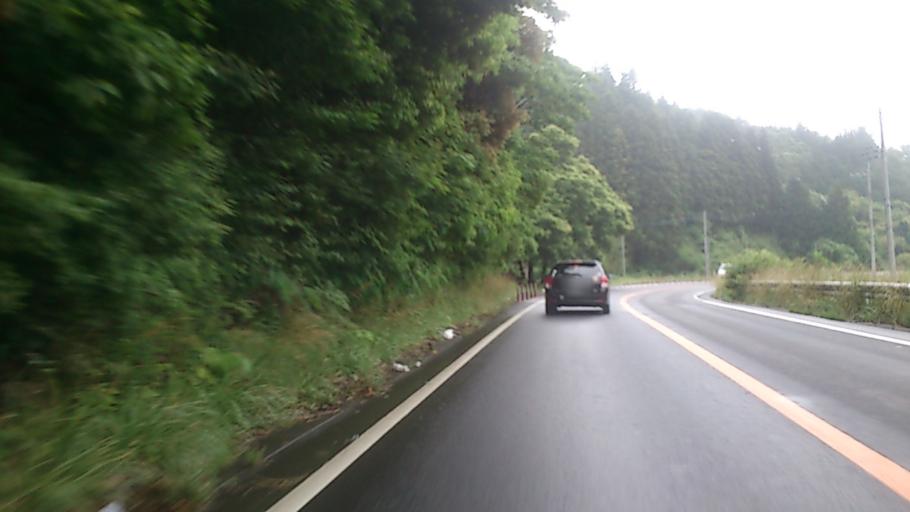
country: JP
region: Tochigi
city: Karasuyama
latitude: 36.6836
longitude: 140.2294
